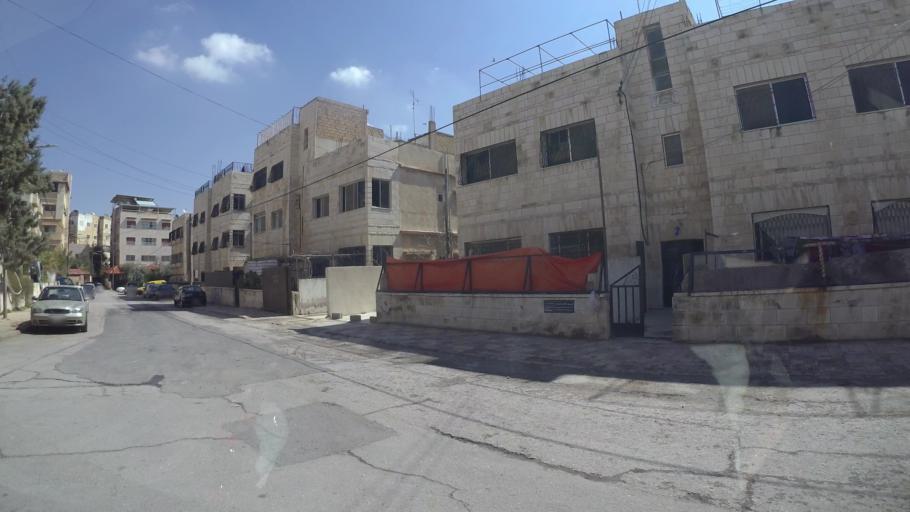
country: JO
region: Amman
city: Amman
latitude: 31.9752
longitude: 35.9890
